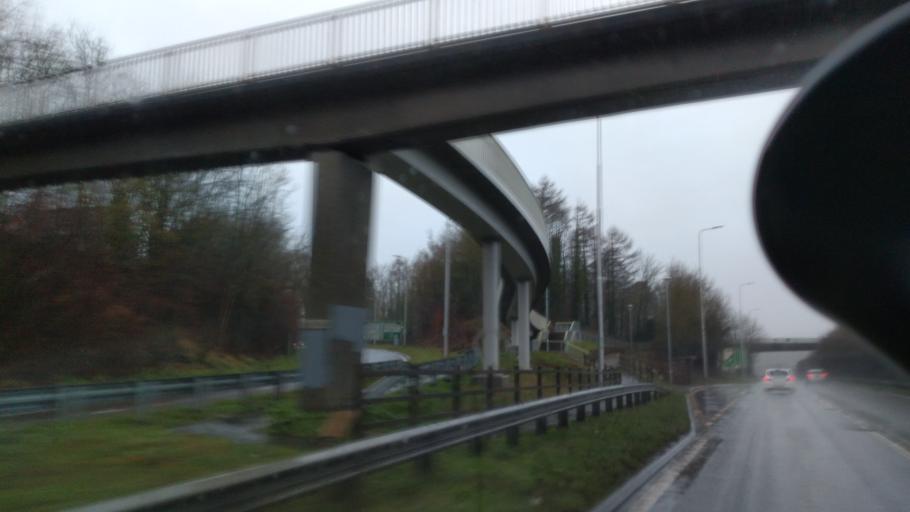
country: GB
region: England
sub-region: Brighton and Hove
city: Rottingdean
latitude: 50.8635
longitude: -0.0782
